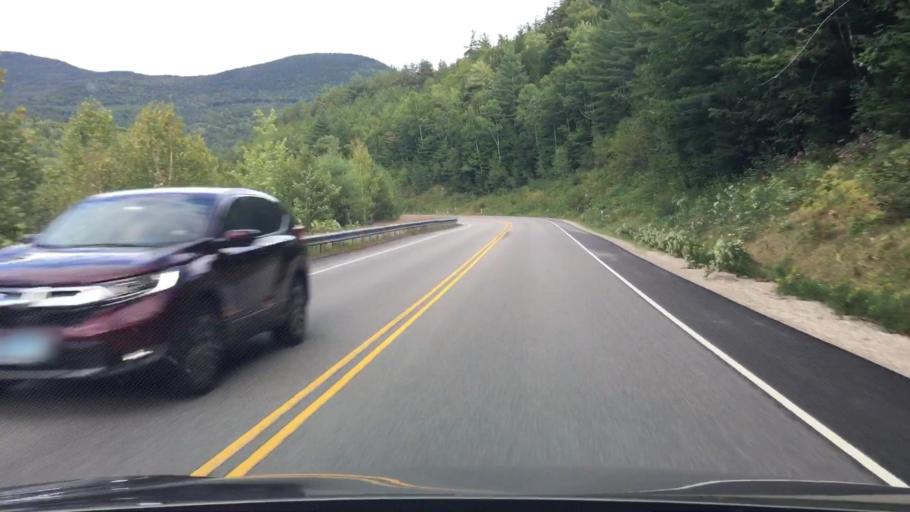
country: US
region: New Hampshire
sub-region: Carroll County
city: North Conway
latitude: 44.0149
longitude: -71.2566
